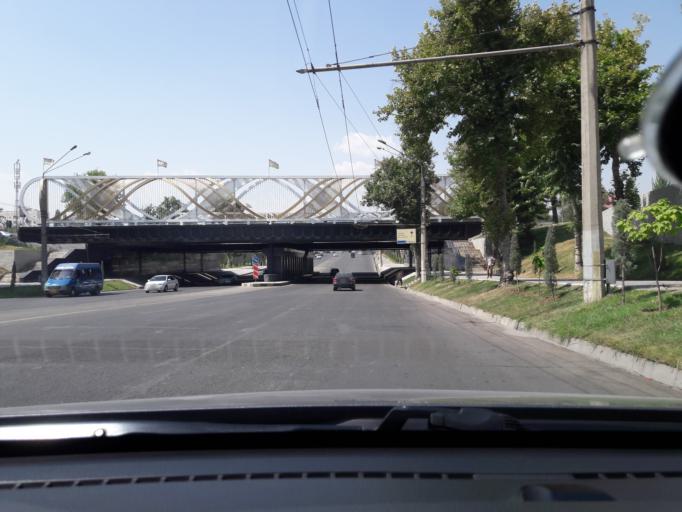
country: TJ
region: Dushanbe
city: Dushanbe
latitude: 38.5684
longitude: 68.7549
